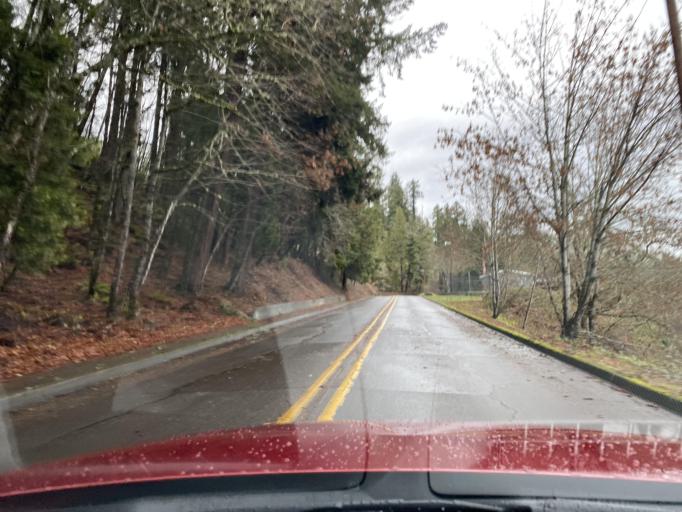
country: US
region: Oregon
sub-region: Lane County
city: Oakridge
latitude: 43.7512
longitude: -122.4877
